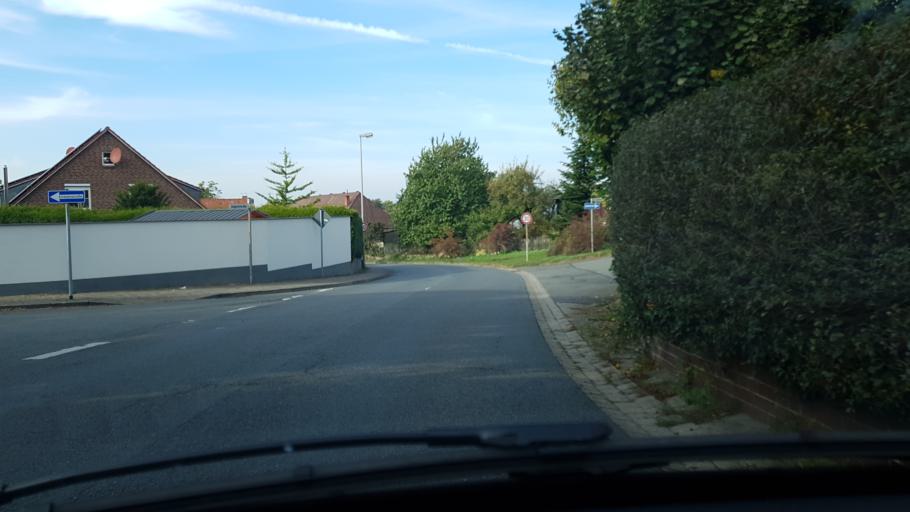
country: DE
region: Lower Saxony
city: Weyhausen
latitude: 52.3980
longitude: 10.6984
